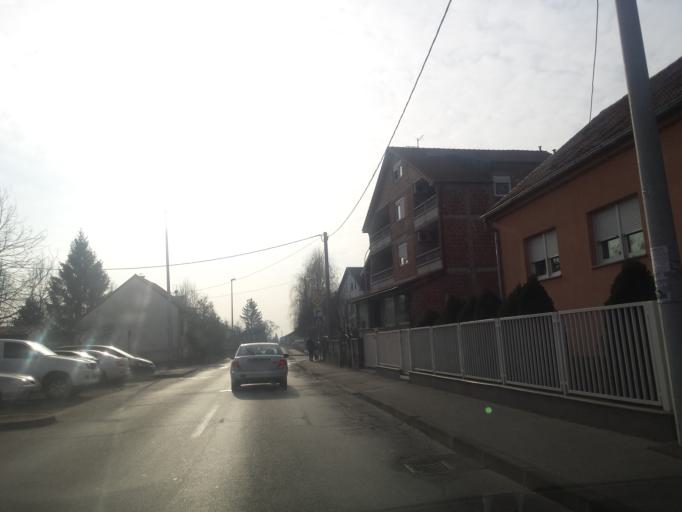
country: HR
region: Grad Zagreb
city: Jankomir
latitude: 45.7909
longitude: 15.9055
